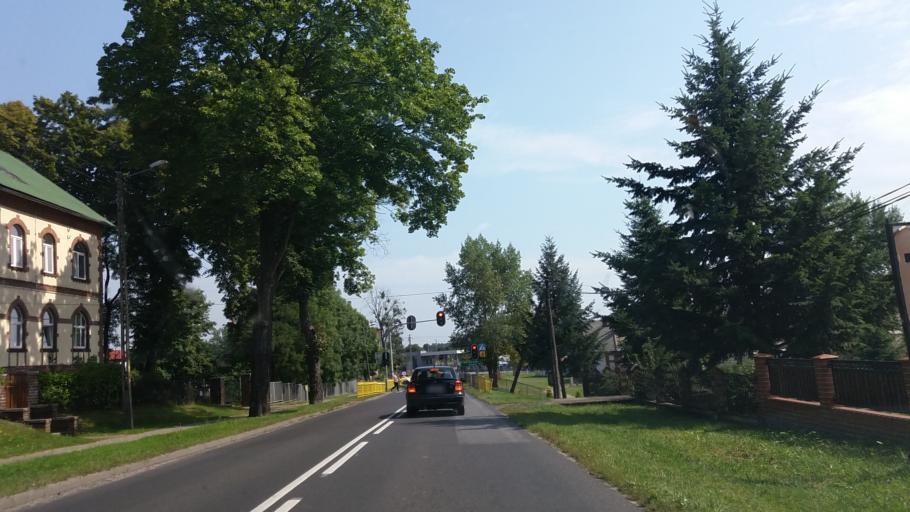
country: PL
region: Lubusz
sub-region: Powiat strzelecko-drezdenecki
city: Zwierzyn
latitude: 52.8373
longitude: 15.5806
